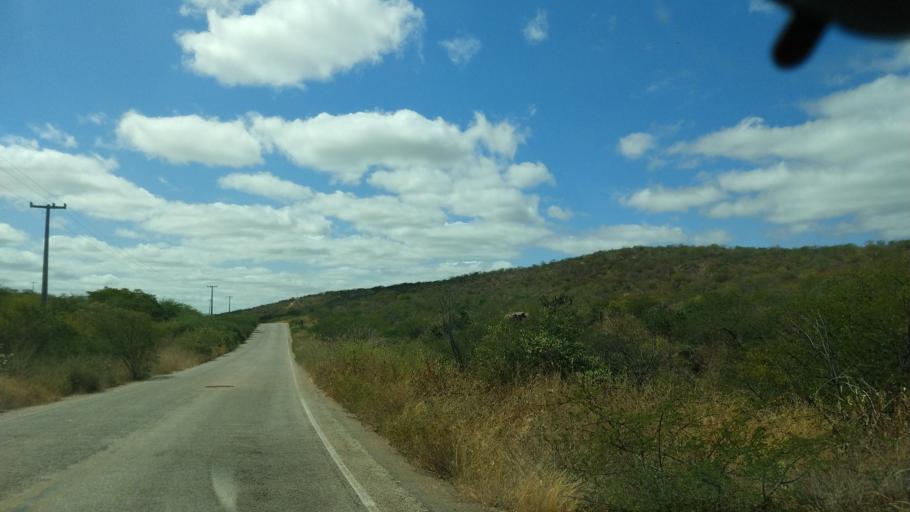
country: BR
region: Rio Grande do Norte
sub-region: Currais Novos
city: Currais Novos
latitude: -6.2619
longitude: -36.5833
